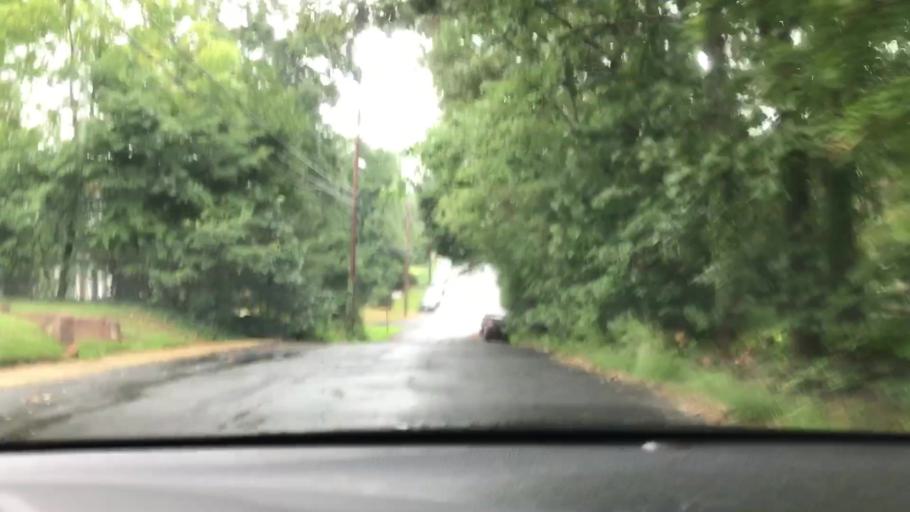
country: US
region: Virginia
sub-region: Arlington County
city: Arlington
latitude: 38.8772
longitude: -77.0937
